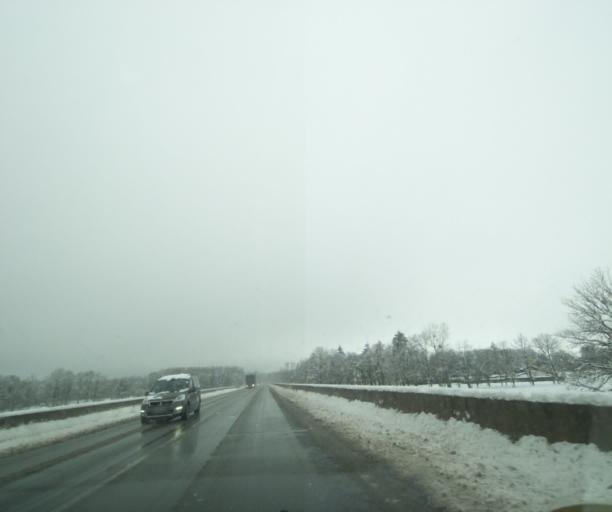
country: FR
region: Champagne-Ardenne
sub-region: Departement de la Haute-Marne
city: Villiers-en-Lieu
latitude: 48.5766
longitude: 4.8701
